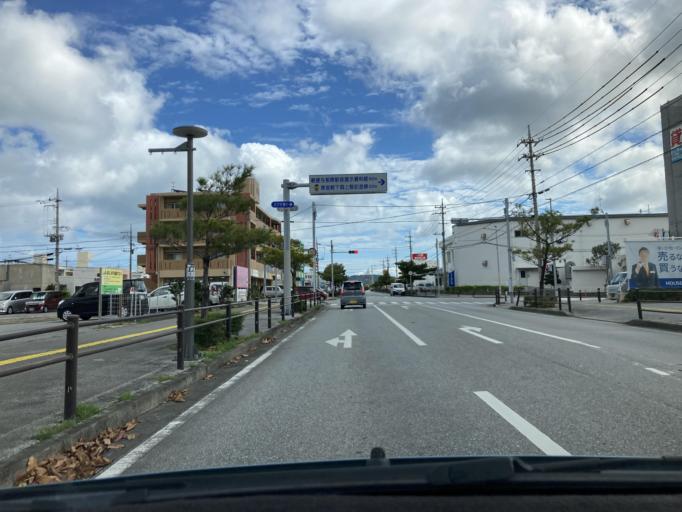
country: JP
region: Okinawa
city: Ginowan
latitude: 26.2070
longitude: 127.7595
